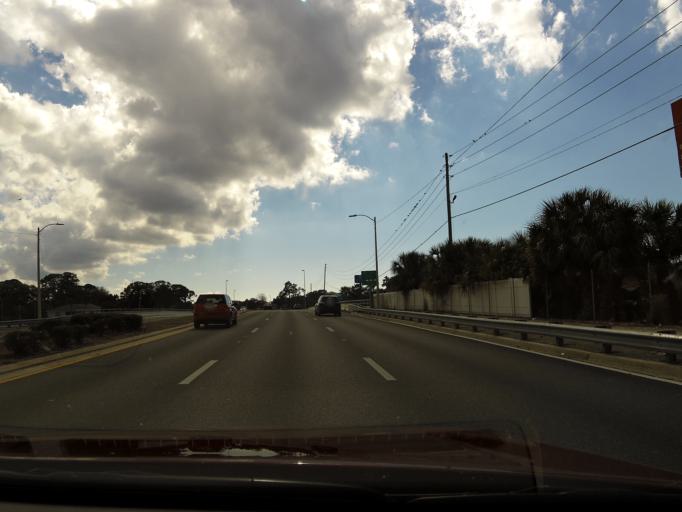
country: US
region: Florida
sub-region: Pasco County
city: Port Richey
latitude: 28.2704
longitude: -82.7257
